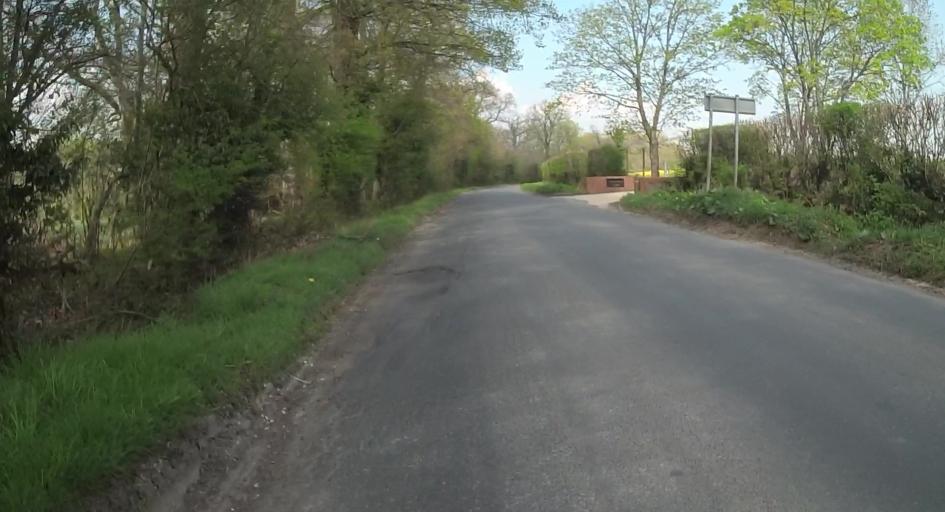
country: GB
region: England
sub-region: Hampshire
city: Basingstoke
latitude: 51.3154
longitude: -1.0822
